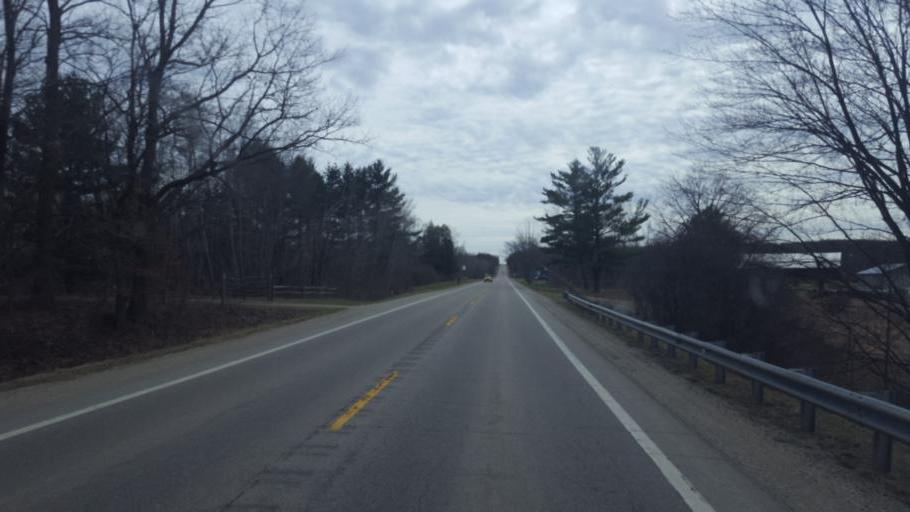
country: US
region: Michigan
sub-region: Isabella County
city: Lake Isabella
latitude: 43.6932
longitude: -85.1467
